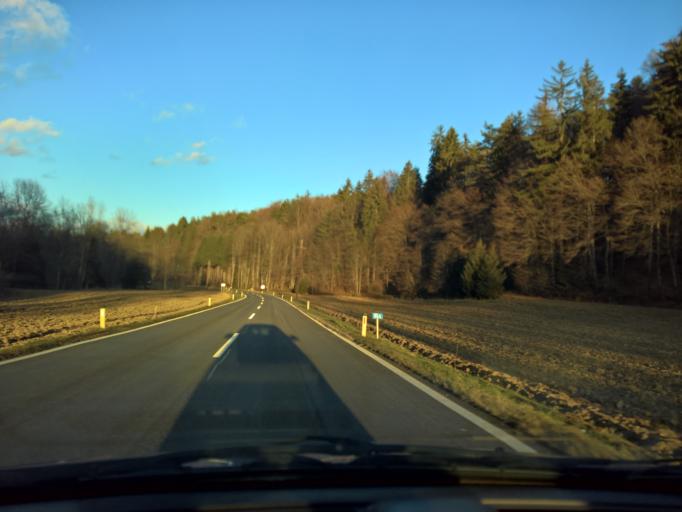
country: AT
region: Styria
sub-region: Politischer Bezirk Leibnitz
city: Leutschach
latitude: 46.7021
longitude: 15.5030
